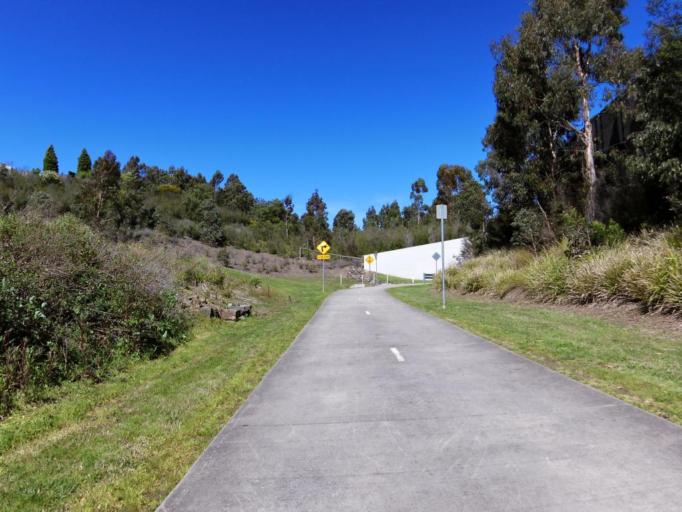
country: AU
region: Victoria
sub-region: Greater Dandenong
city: Noble Park North
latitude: -37.9368
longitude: 145.2084
